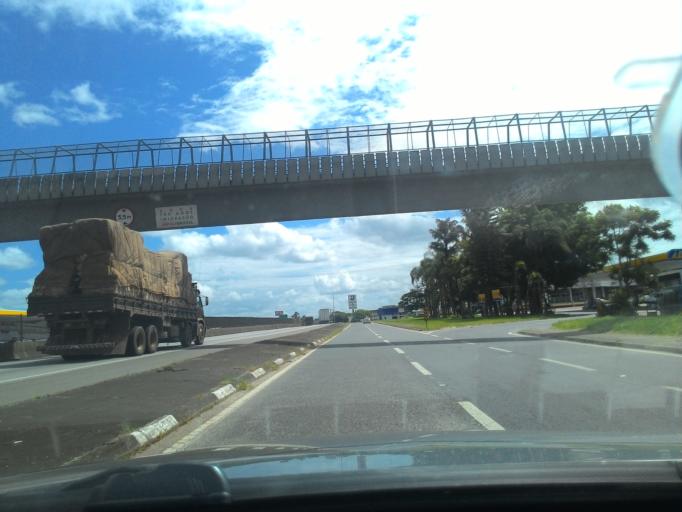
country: BR
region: Sao Paulo
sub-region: Registro
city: Registro
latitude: -24.5005
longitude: -47.8453
